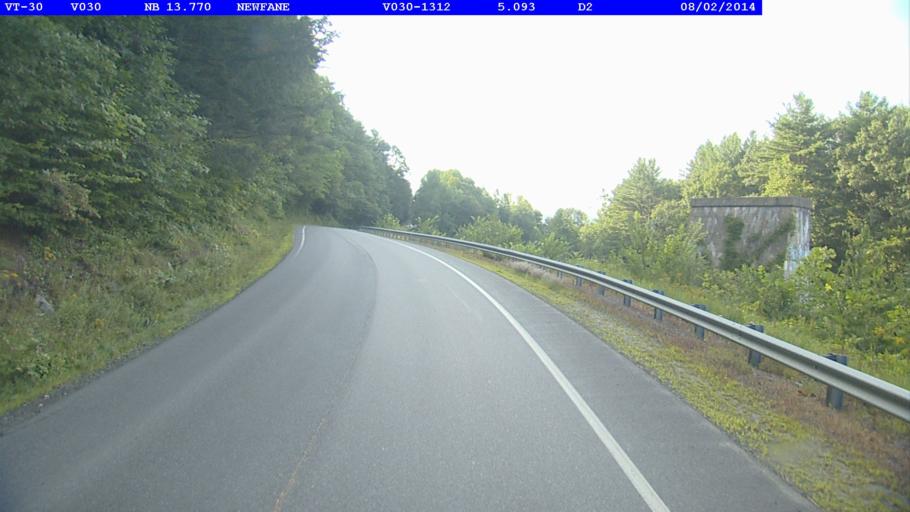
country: US
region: Vermont
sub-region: Windham County
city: Newfane
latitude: 43.0129
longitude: -72.6499
